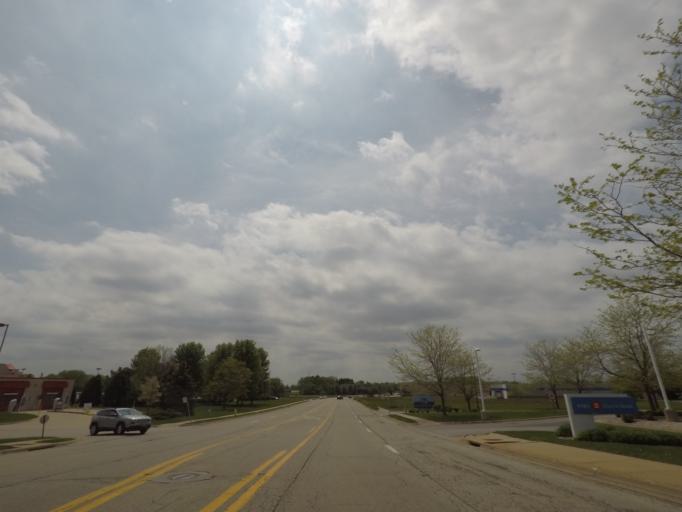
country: US
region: Illinois
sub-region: Winnebago County
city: Machesney Park
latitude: 42.3074
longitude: -88.9776
